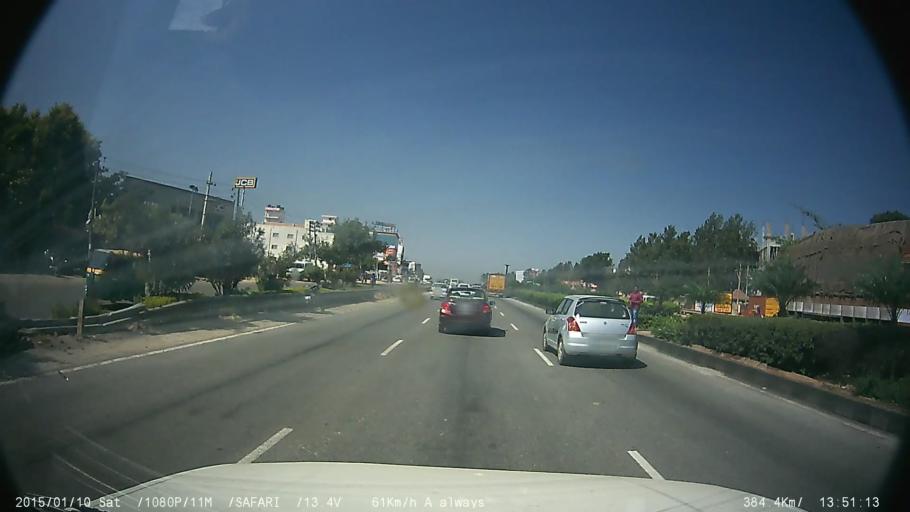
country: IN
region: Karnataka
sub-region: Bangalore Urban
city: Anekal
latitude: 12.8318
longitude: 77.6807
